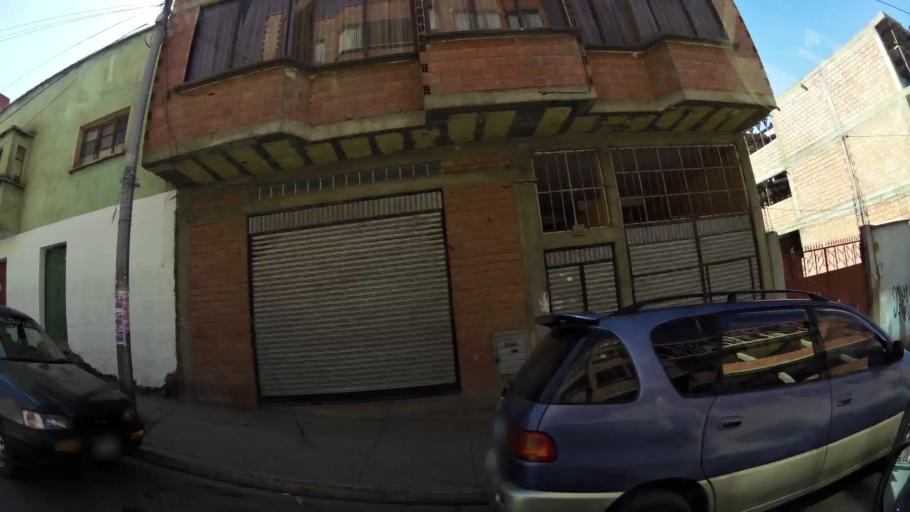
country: BO
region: La Paz
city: La Paz
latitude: -16.4925
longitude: -68.1568
